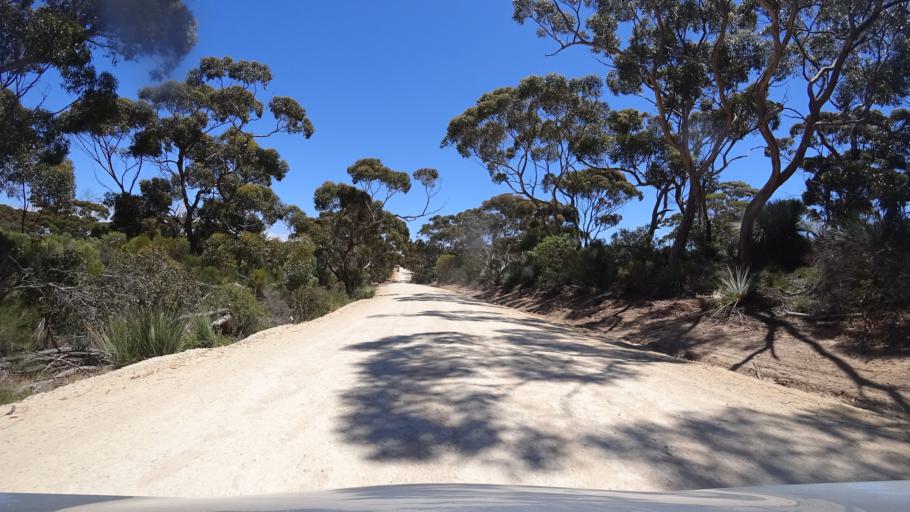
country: AU
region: South Australia
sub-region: Kangaroo Island
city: Kingscote
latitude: -35.6495
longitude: 137.1811
